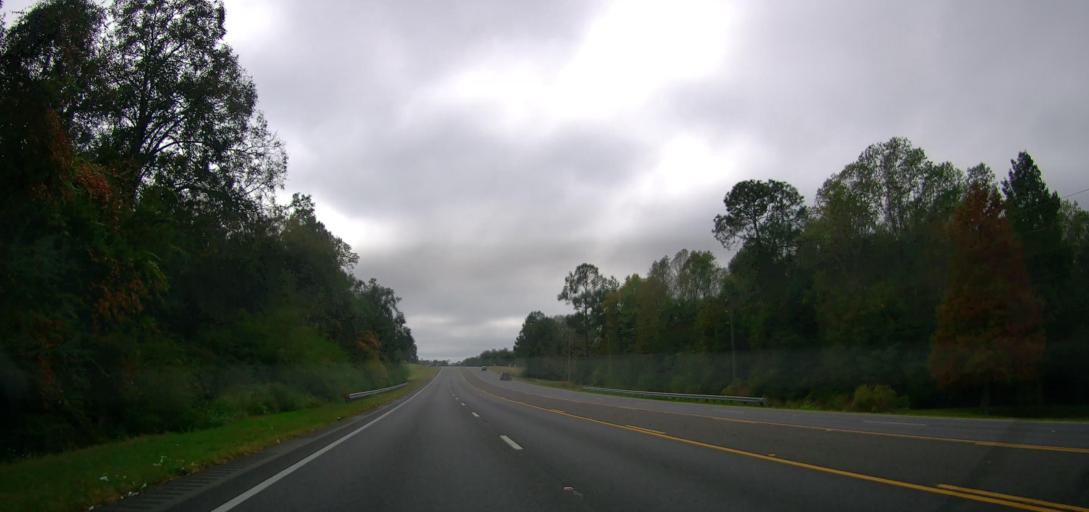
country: US
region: Georgia
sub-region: Thomas County
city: Thomasville
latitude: 30.9601
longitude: -83.8945
